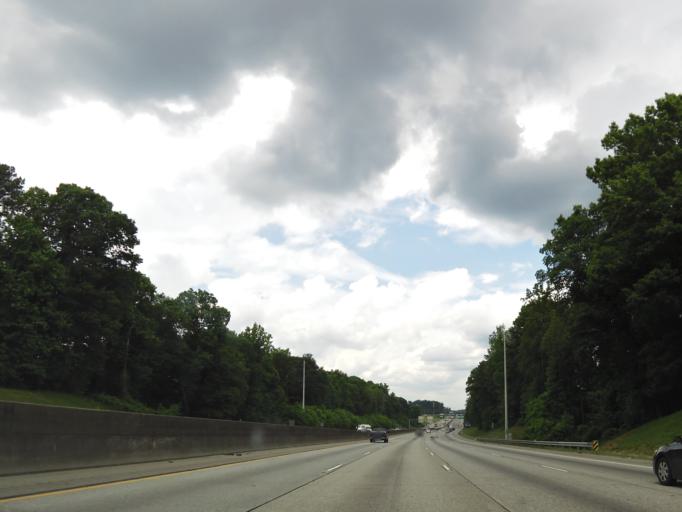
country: US
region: Georgia
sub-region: Fulton County
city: College Park
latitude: 33.6470
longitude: -84.4974
